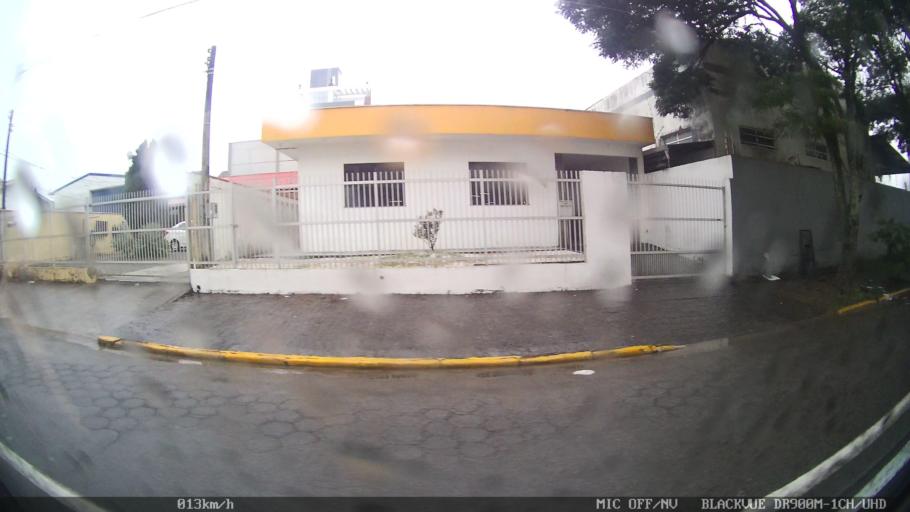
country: BR
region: Santa Catarina
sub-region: Itajai
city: Itajai
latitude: -26.9110
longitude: -48.6818
